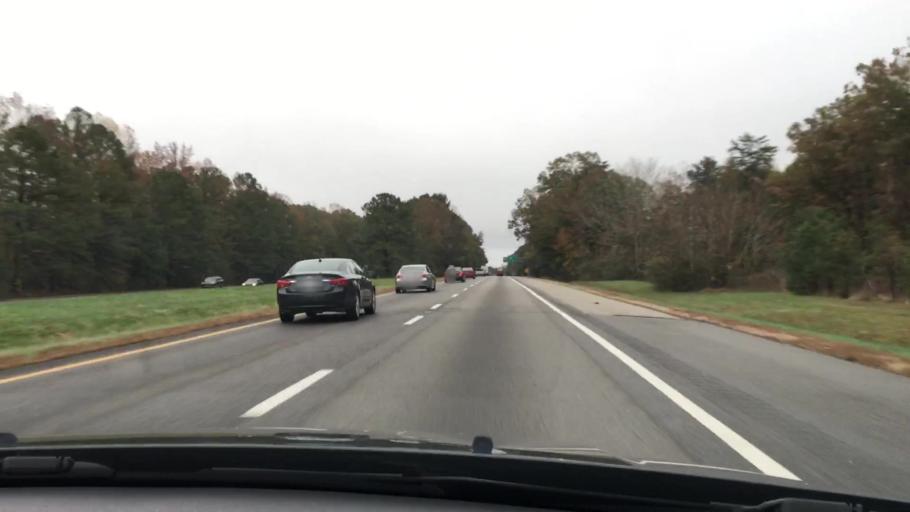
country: US
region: Virginia
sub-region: James City County
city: Williamsburg
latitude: 37.3913
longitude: -76.7699
